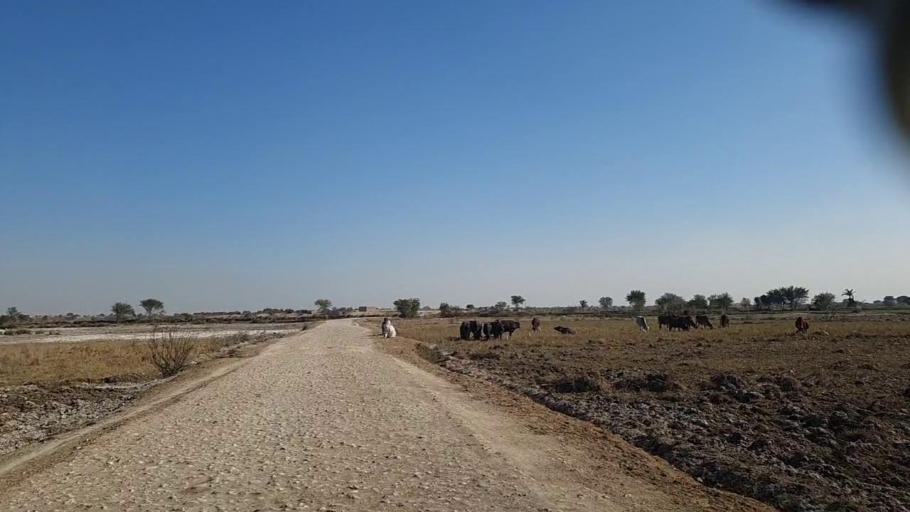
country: PK
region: Sindh
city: Khairpur
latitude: 27.9259
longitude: 69.7350
